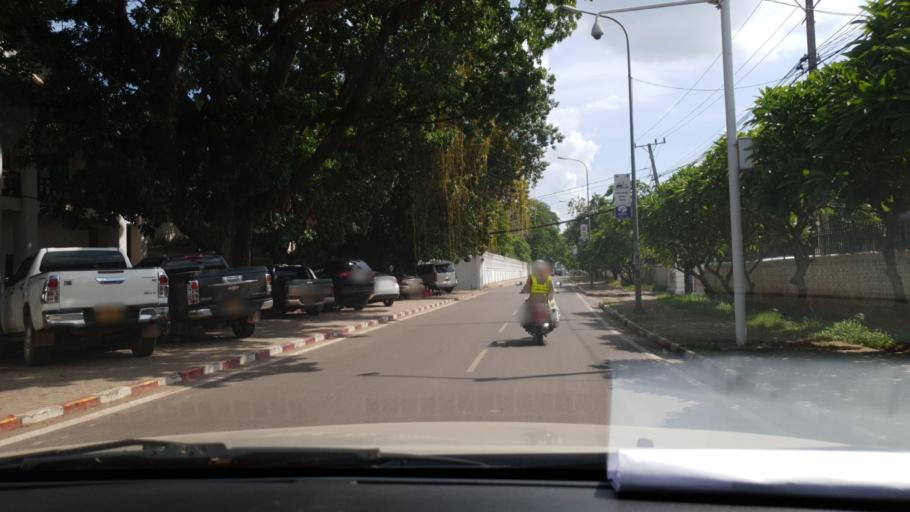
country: LA
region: Vientiane
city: Vientiane
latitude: 17.9629
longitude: 102.6137
